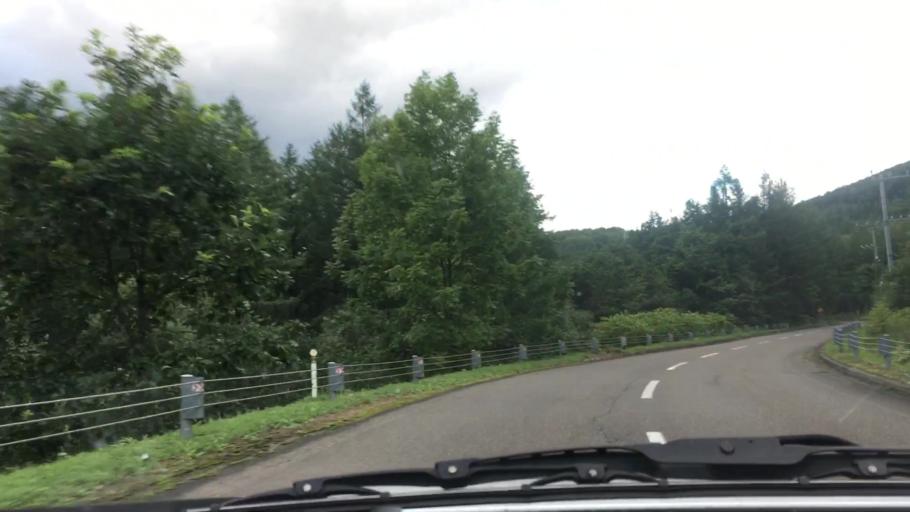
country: JP
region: Hokkaido
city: Otofuke
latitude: 43.1532
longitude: 142.8583
